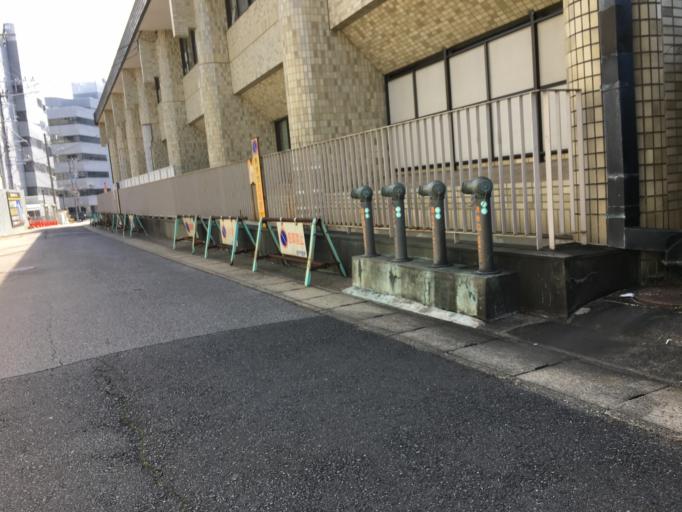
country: JP
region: Chiba
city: Matsudo
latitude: 35.7882
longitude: 139.9035
